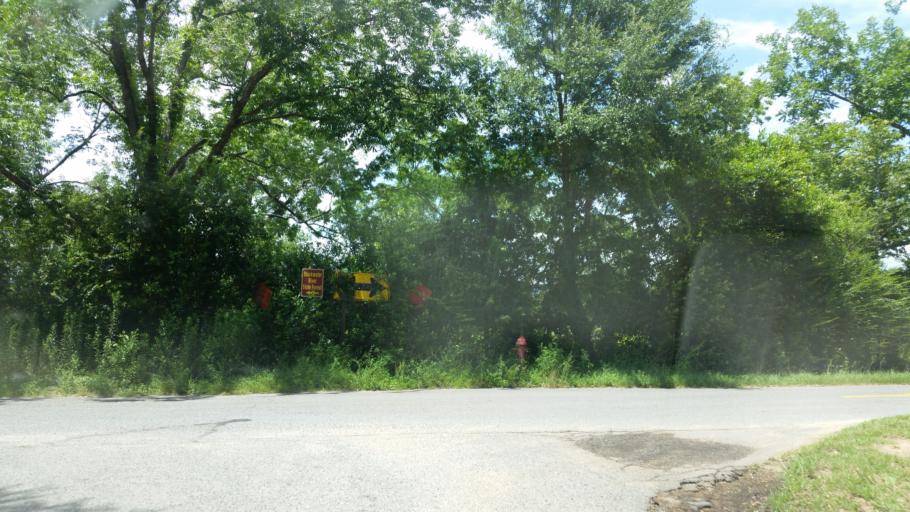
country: US
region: Florida
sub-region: Okaloosa County
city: Crestview
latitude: 30.7134
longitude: -86.7582
